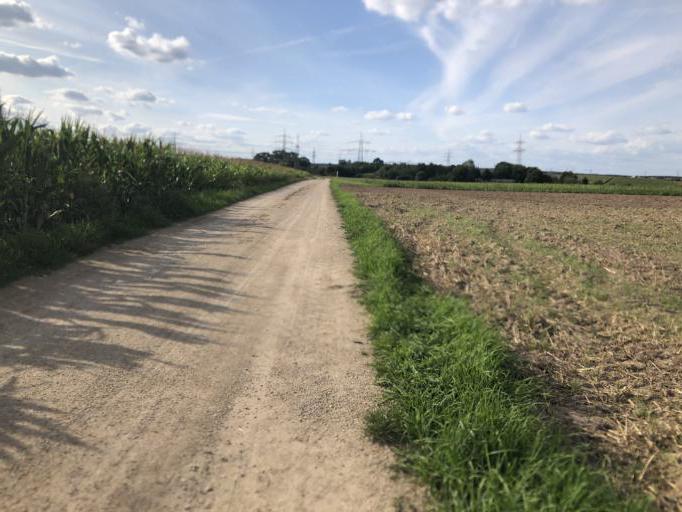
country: DE
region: Bavaria
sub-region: Regierungsbezirk Mittelfranken
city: Erlangen
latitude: 49.5757
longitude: 10.9564
